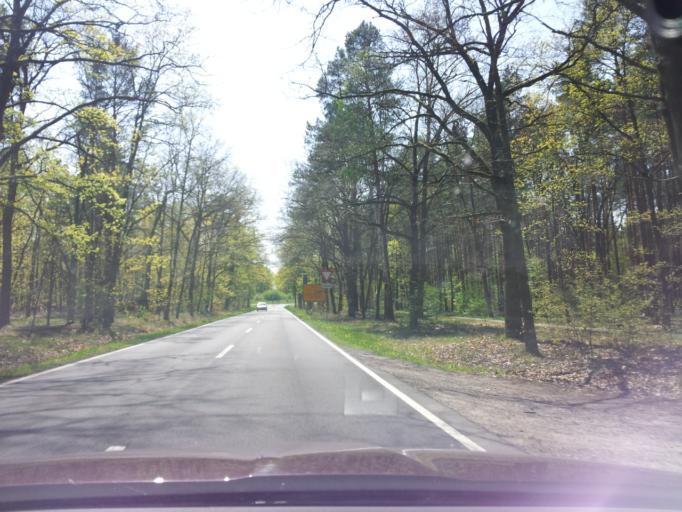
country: DE
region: Brandenburg
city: Stahnsdorf
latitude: 52.3440
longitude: 13.1590
